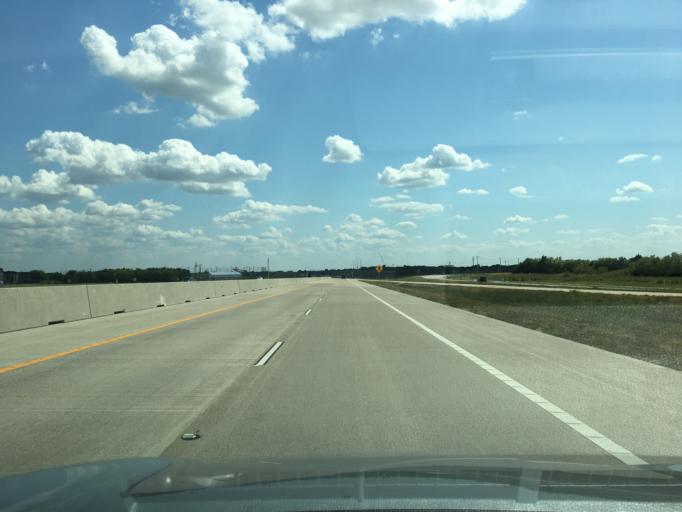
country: US
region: Texas
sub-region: Tarrant County
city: Mansfield
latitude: 32.5676
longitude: -97.0834
